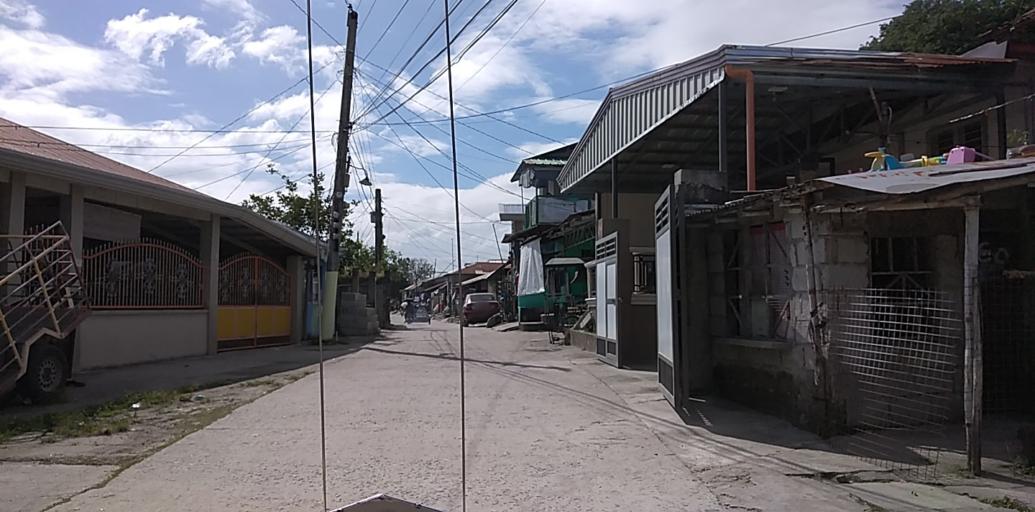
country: PH
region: Central Luzon
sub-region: Province of Pampanga
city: Porac
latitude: 15.0778
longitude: 120.5318
